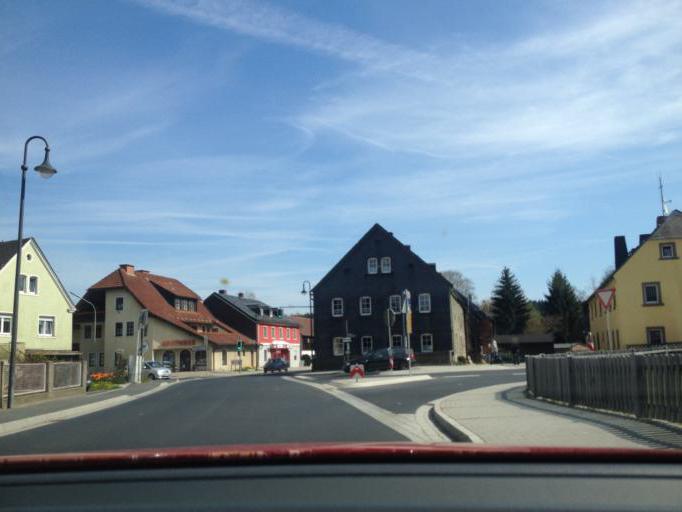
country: DE
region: Bavaria
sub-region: Upper Franconia
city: Roslau
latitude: 50.0816
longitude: 11.9770
